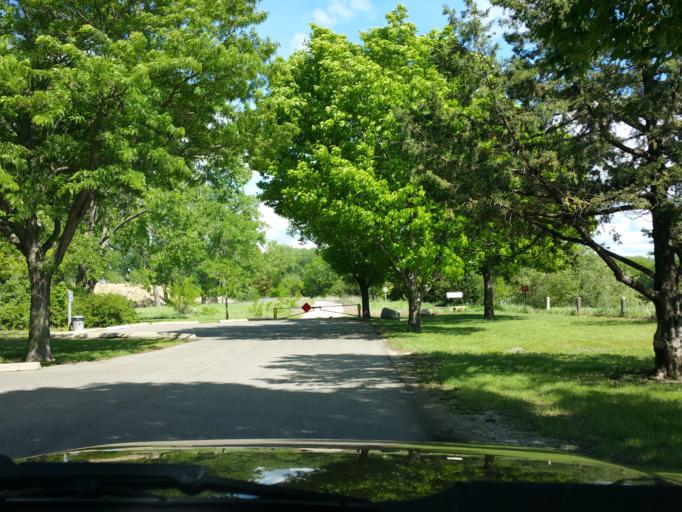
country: US
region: Kansas
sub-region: Riley County
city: Manhattan
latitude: 39.2499
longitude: -96.5967
